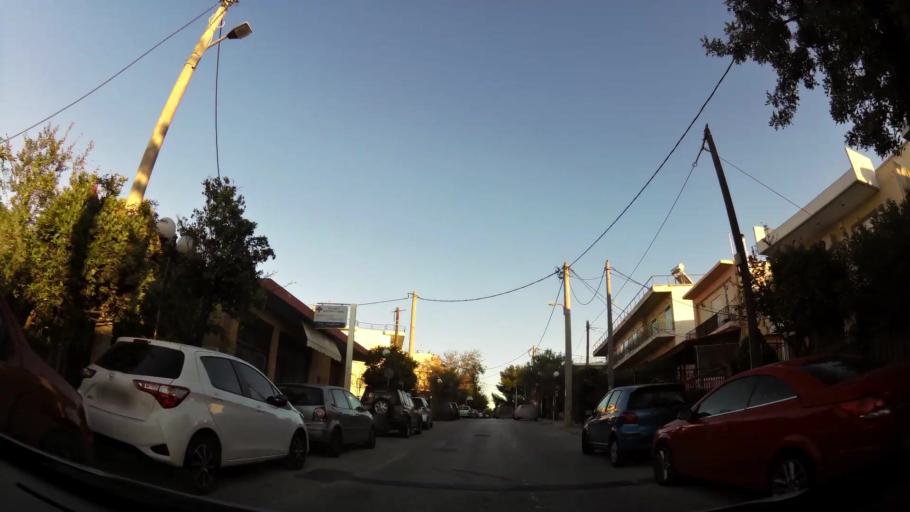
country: GR
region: Attica
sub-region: Nomarchia Athinas
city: Lykovrysi
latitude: 38.0690
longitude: 23.7838
